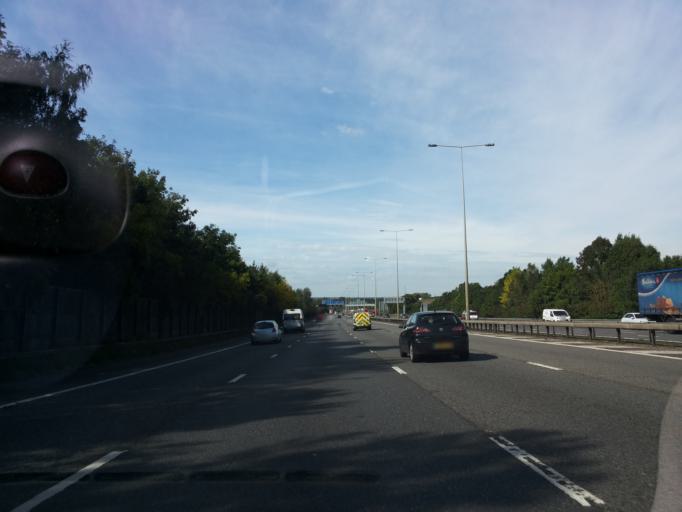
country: GB
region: England
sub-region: Kent
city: Boxley
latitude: 51.2920
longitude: 0.5344
